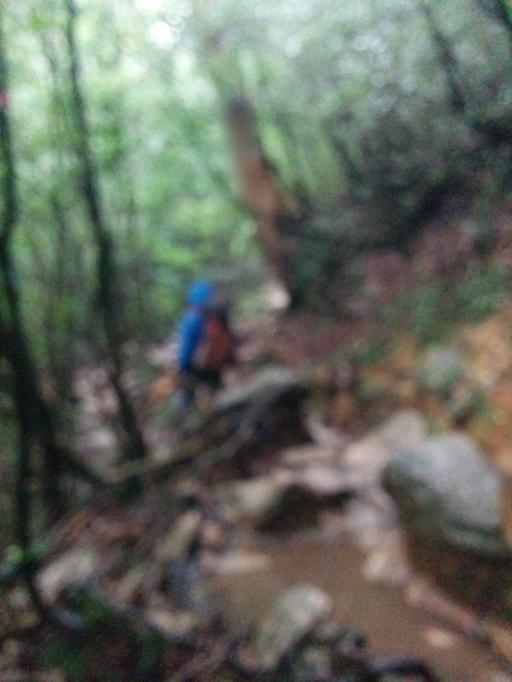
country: JP
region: Kagoshima
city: Nishinoomote
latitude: 30.3532
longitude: 130.5399
